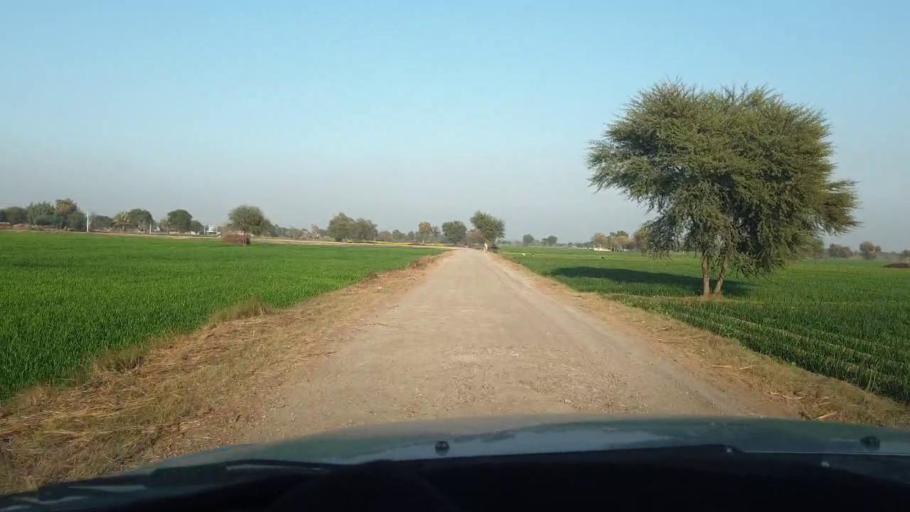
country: PK
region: Sindh
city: Mirpur Mathelo
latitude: 27.9811
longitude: 69.6270
